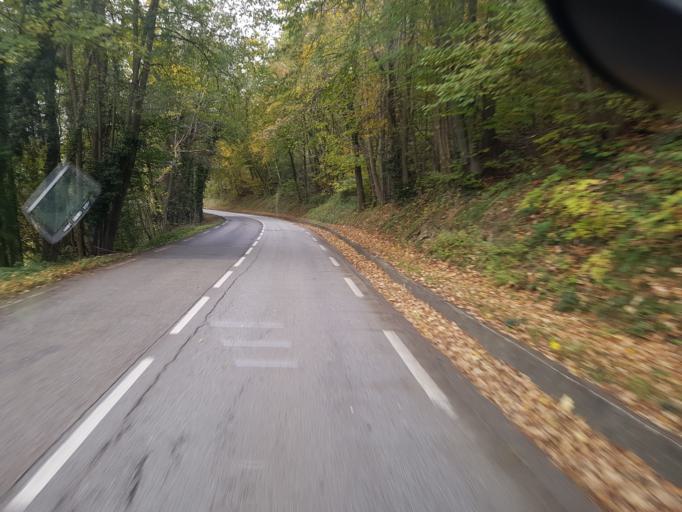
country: FR
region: Rhone-Alpes
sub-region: Departement de l'Isere
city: Le Gua
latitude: 44.9711
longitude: 5.6409
